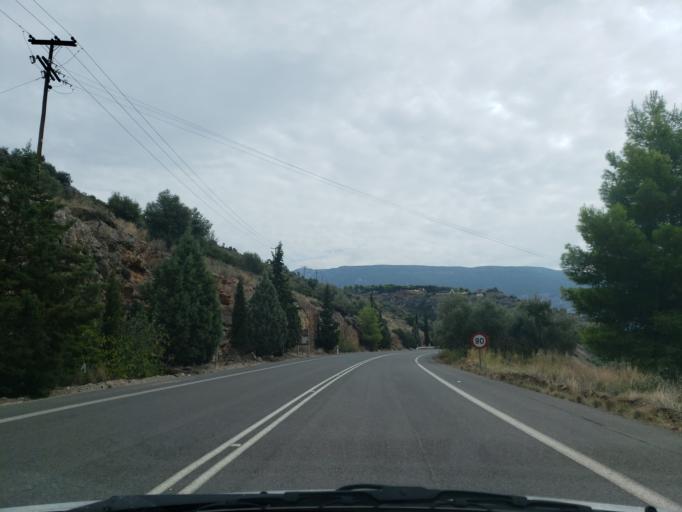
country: GR
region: Central Greece
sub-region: Nomos Fokidos
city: Delphi
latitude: 38.4768
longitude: 22.4536
